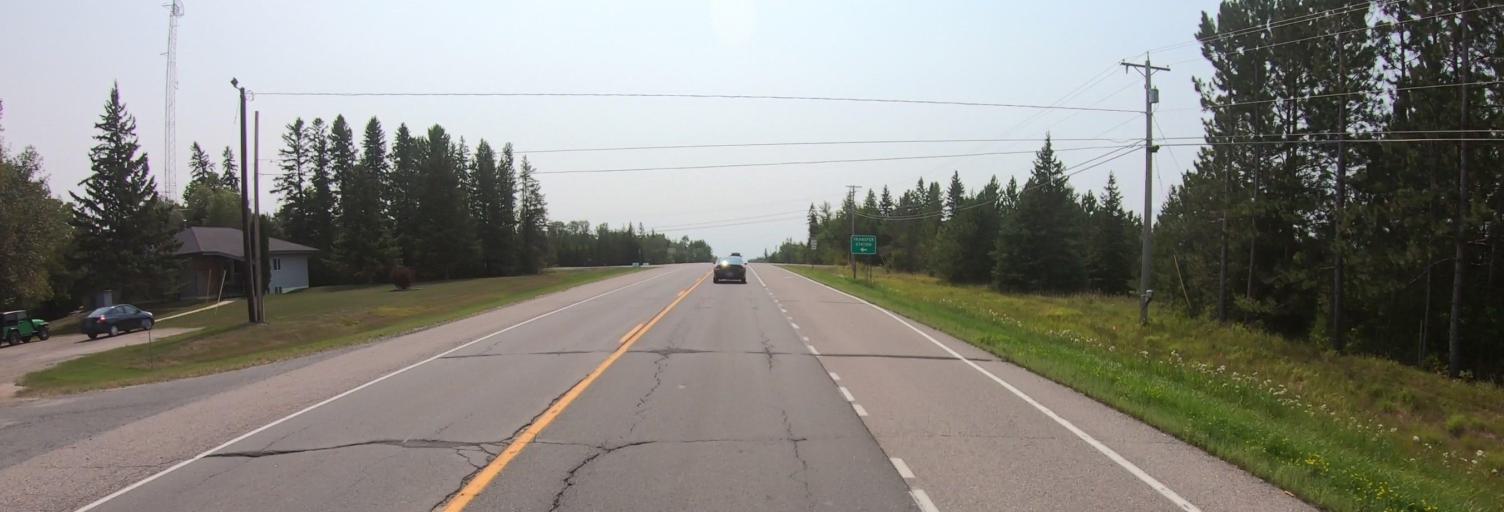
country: US
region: Minnesota
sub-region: Koochiching County
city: International Falls
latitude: 48.5712
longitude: -93.4400
